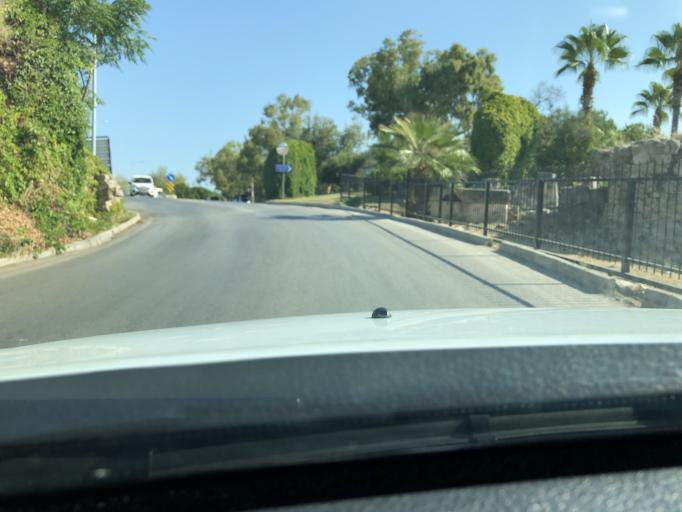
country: TR
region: Antalya
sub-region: Manavgat
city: Side
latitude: 36.7720
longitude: 31.3946
